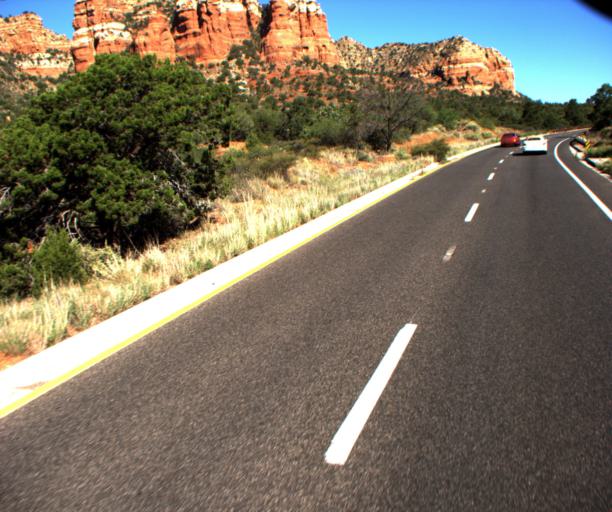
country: US
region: Arizona
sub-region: Yavapai County
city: Village of Oak Creek (Big Park)
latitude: 34.7987
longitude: -111.7673
